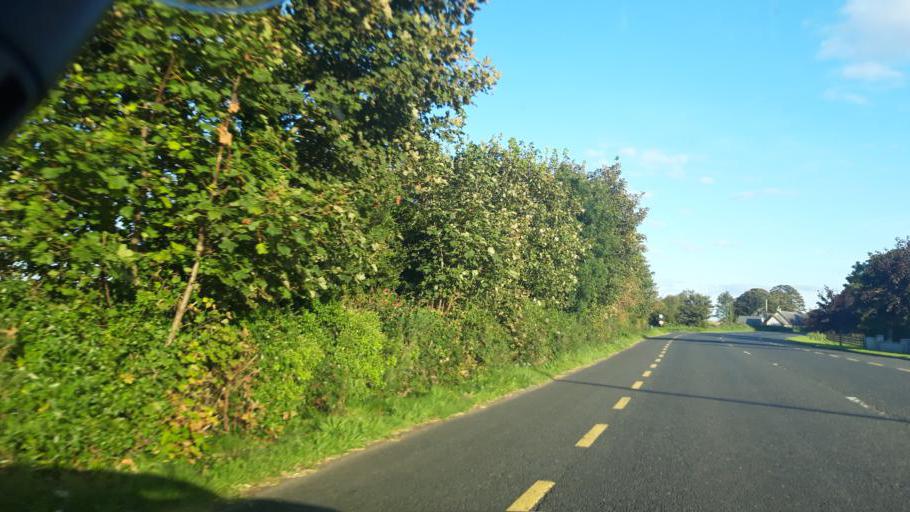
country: IE
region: Leinster
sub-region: Lu
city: Carlingford
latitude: 54.0259
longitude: -6.1518
